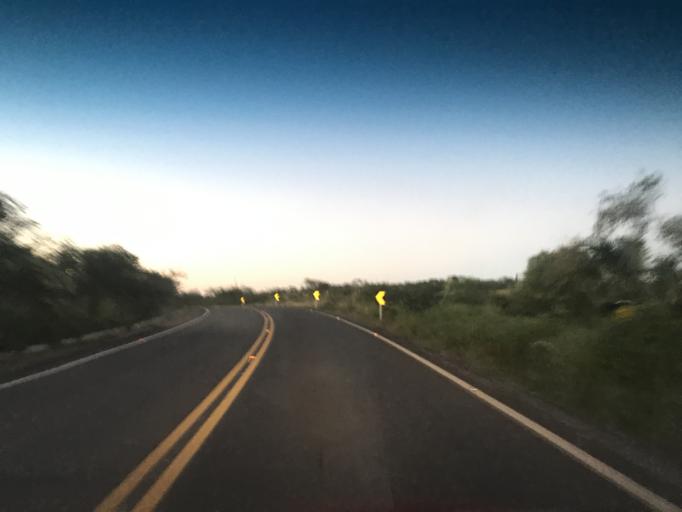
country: BR
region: Bahia
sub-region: Castro Alves
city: Castro Alves
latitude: -12.7508
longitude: -39.4060
